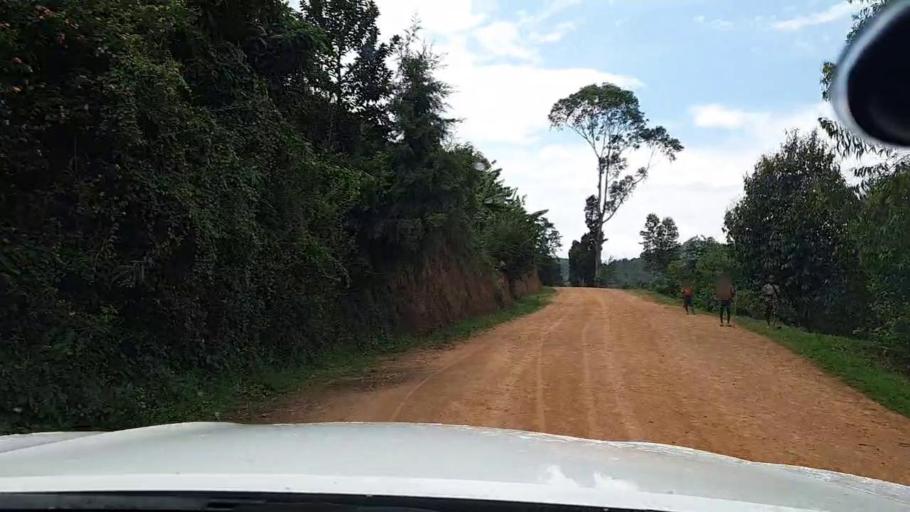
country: RW
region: Western Province
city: Kibuye
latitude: -2.1115
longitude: 29.4204
